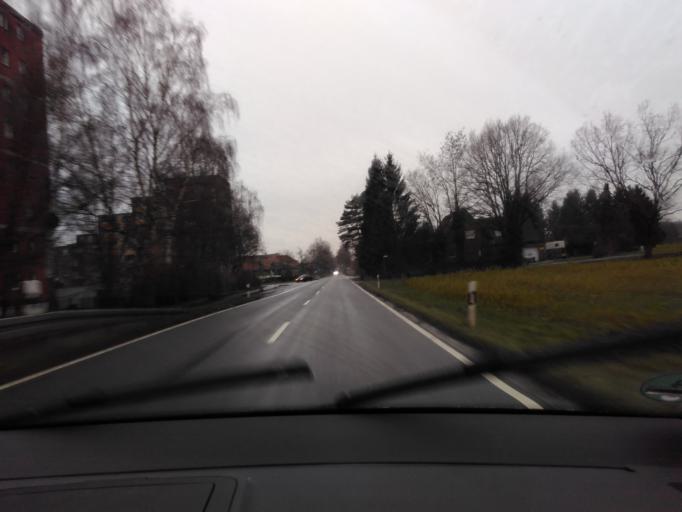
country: DE
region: North Rhine-Westphalia
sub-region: Regierungsbezirk Detmold
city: Verl
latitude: 51.8898
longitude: 8.4848
